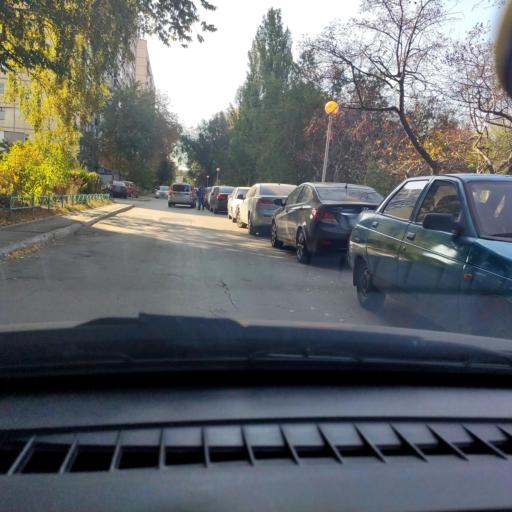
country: RU
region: Samara
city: Tol'yatti
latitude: 53.5240
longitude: 49.2732
